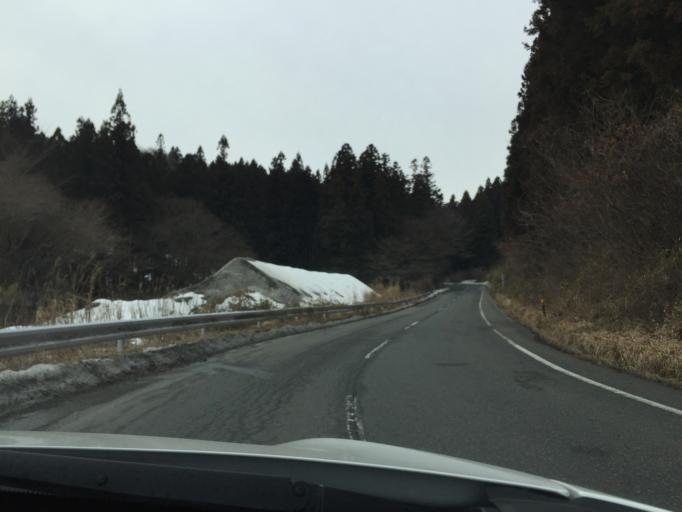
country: JP
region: Fukushima
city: Ishikawa
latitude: 37.1767
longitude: 140.6047
